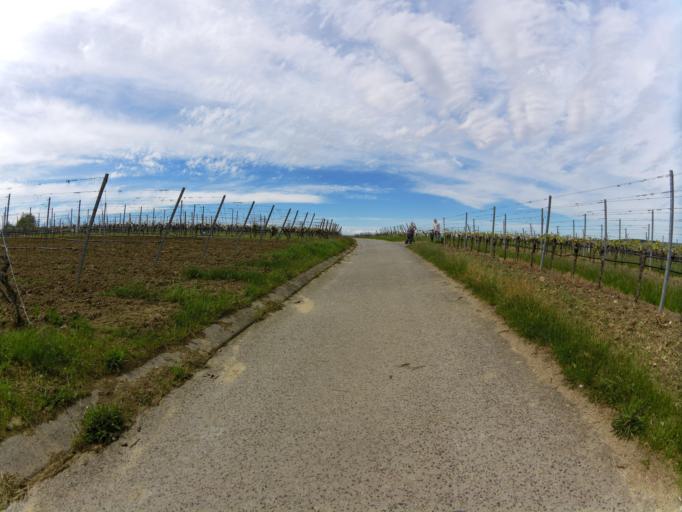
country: DE
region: Bavaria
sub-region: Regierungsbezirk Unterfranken
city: Nordheim
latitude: 49.8536
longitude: 10.2020
